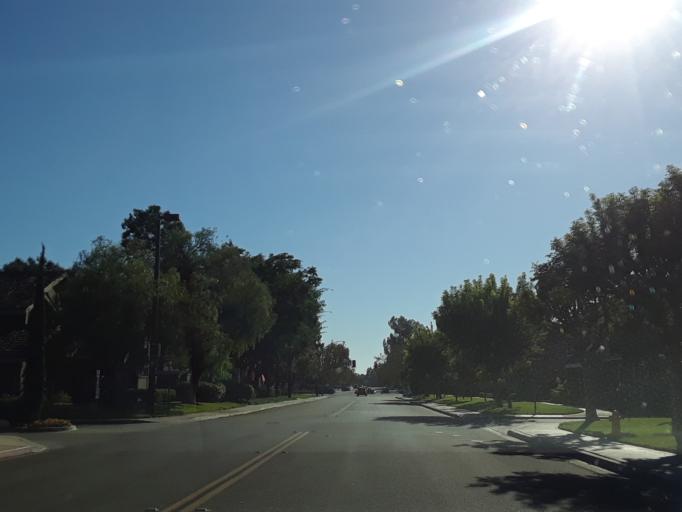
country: US
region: California
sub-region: Orange County
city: Irvine
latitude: 33.6811
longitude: -117.7999
